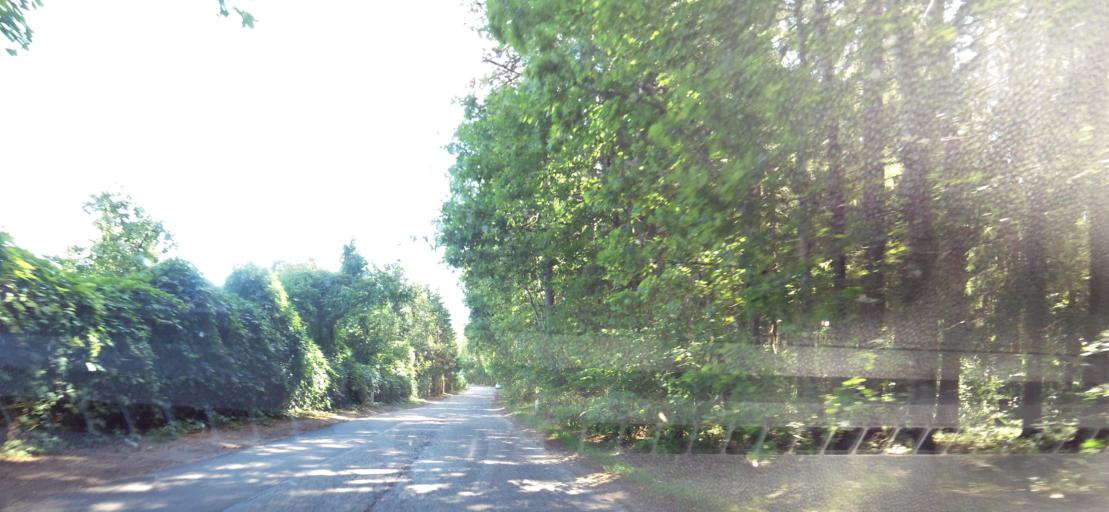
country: LT
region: Vilnius County
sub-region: Vilnius
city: Fabijoniskes
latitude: 54.8210
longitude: 25.3207
